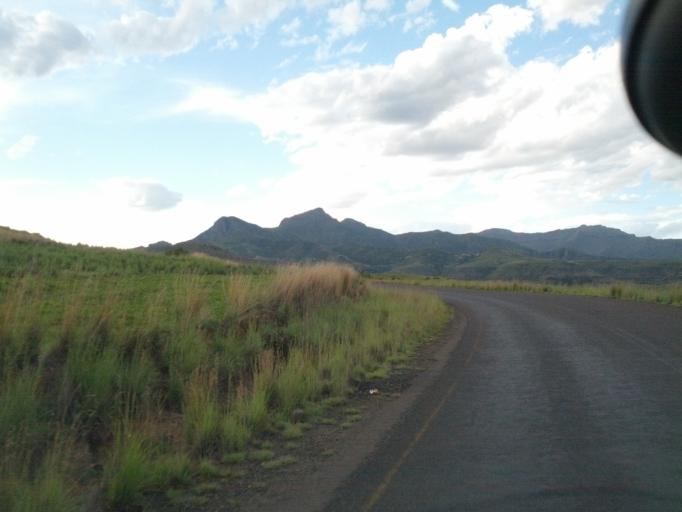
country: LS
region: Qacha's Nek
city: Qacha's Nek
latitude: -30.0661
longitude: 28.6163
